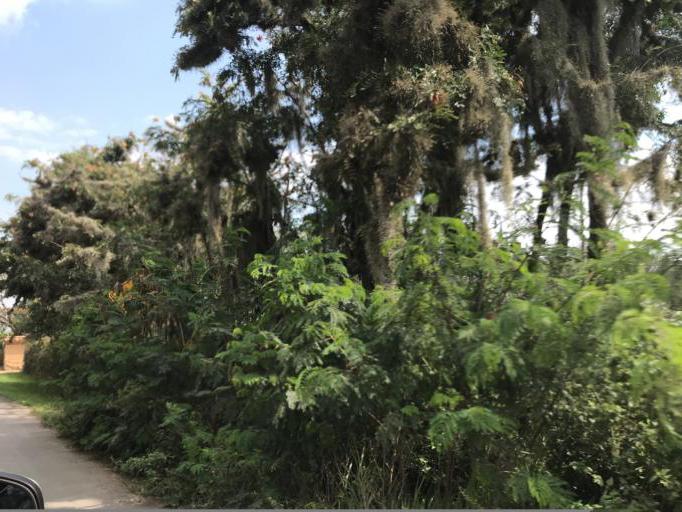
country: CO
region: Boyaca
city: Villa de Leiva
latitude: 5.6534
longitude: -73.5775
